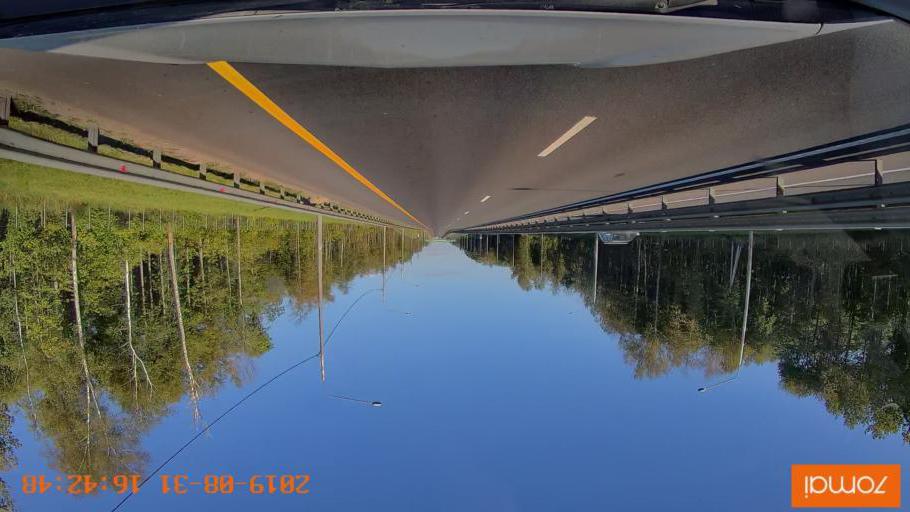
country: RU
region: Kaluga
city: Mstikhino
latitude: 54.5997
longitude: 36.0924
